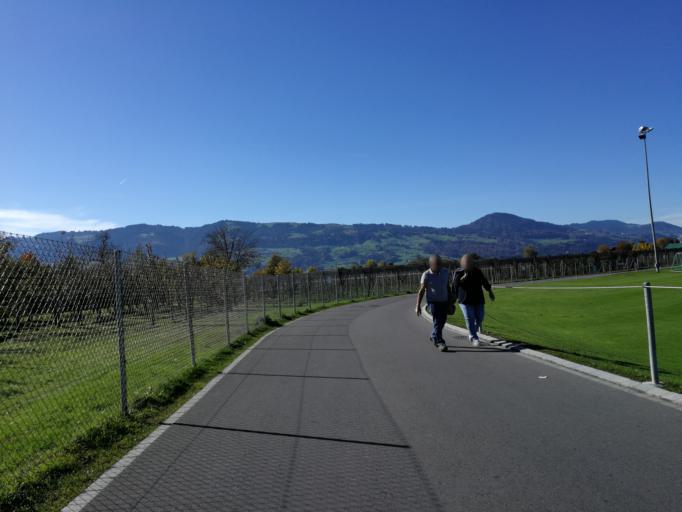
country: CH
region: Saint Gallen
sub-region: Wahlkreis See-Gaster
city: Jona
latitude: 47.2203
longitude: 8.8474
